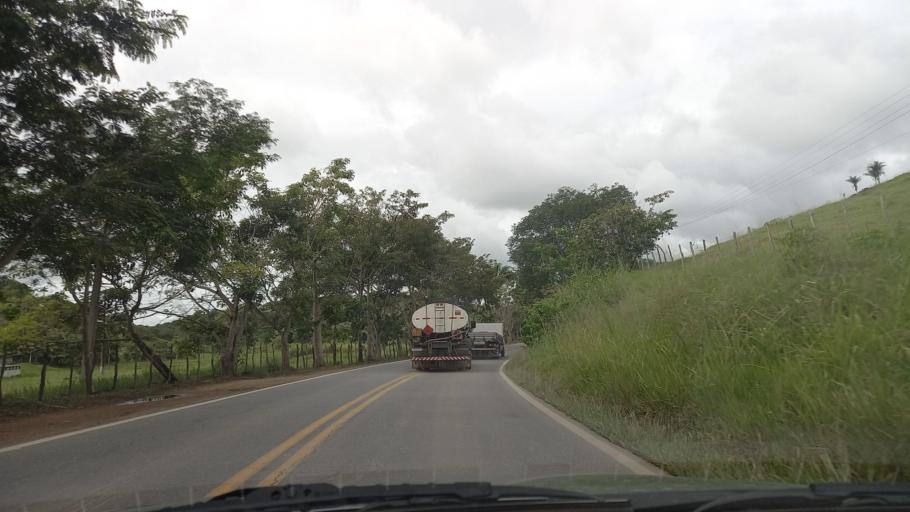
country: BR
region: Pernambuco
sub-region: Canhotinho
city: Canhotinho
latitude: -8.8673
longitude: -36.1925
